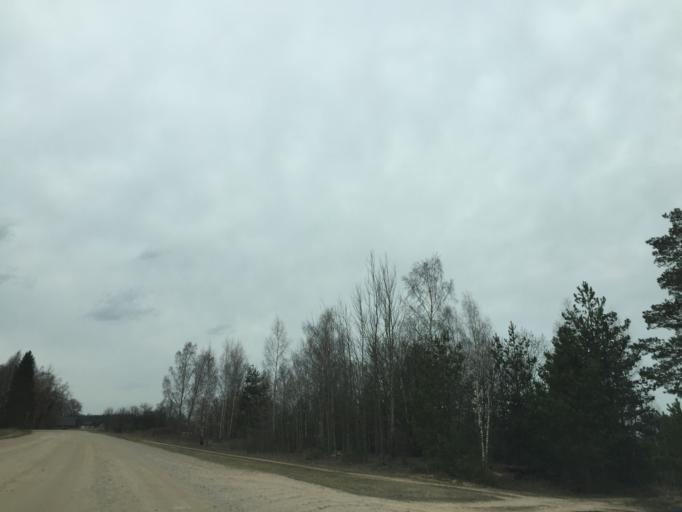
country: LV
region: Livani
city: Livani
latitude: 56.3051
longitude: 26.1697
